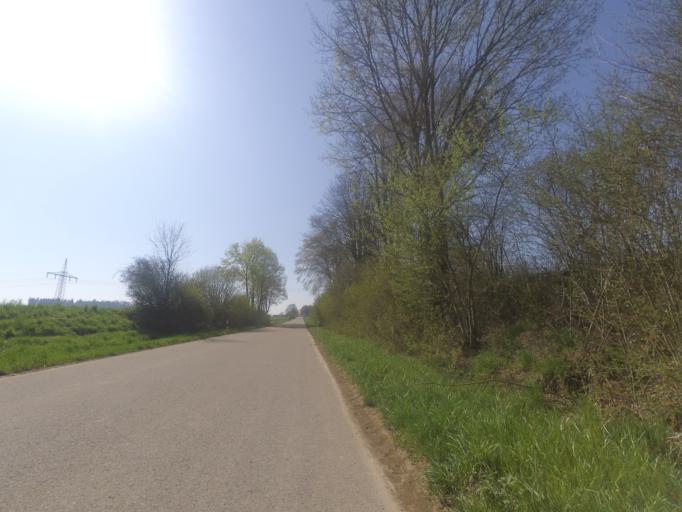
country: DE
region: Bavaria
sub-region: Swabia
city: Pfaffenhofen an der Roth
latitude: 48.3909
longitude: 10.1745
